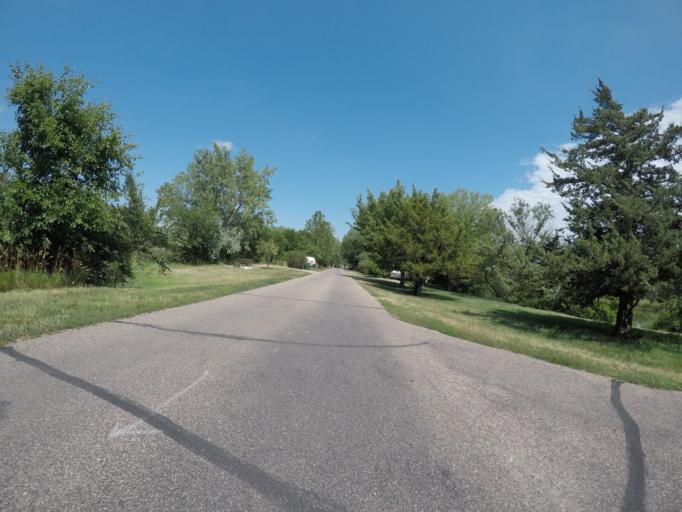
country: US
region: Nebraska
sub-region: Buffalo County
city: Kearney
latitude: 40.6540
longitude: -98.9967
